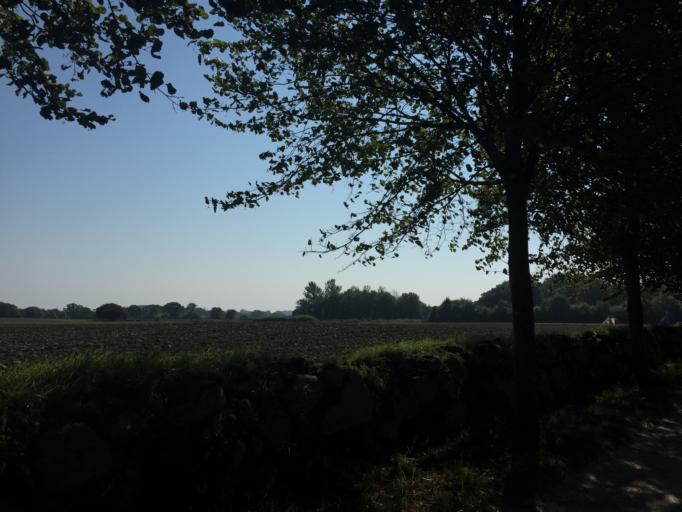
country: DK
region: South Denmark
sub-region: Langeland Kommune
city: Rudkobing
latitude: 54.8473
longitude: 10.7532
